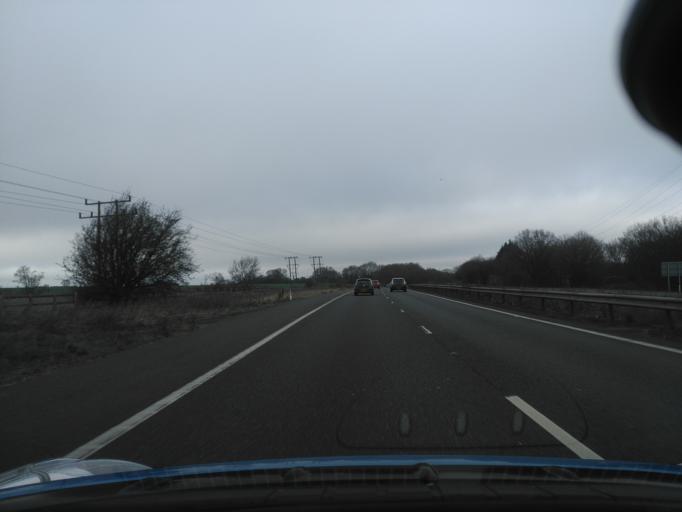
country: GB
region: England
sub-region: Hertfordshire
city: Stevenage
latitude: 51.9043
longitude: -0.2243
